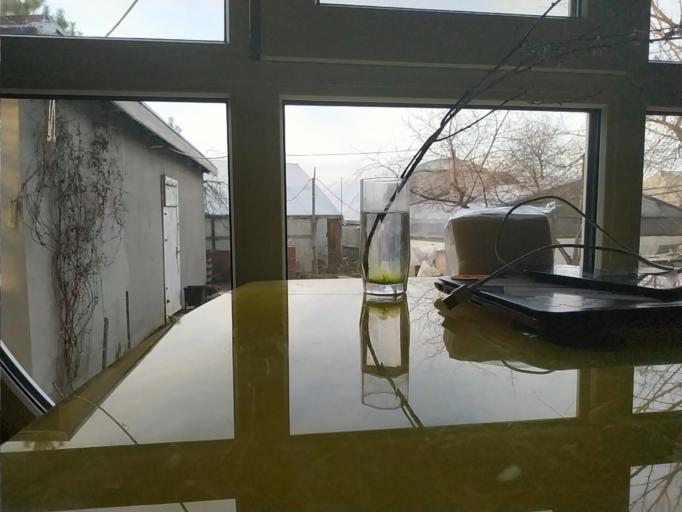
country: RU
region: Republic of Karelia
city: Suoyarvi
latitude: 62.1714
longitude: 32.1313
